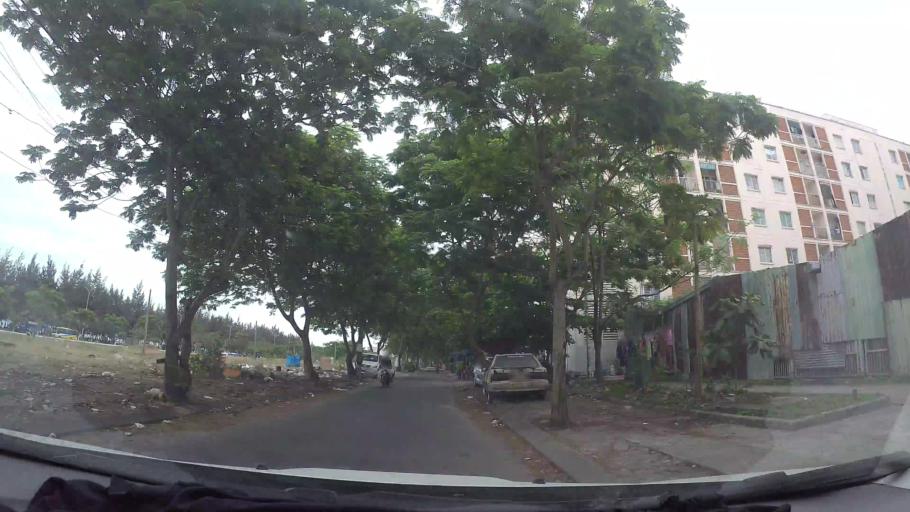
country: VN
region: Da Nang
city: Lien Chieu
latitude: 16.1083
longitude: 108.1331
